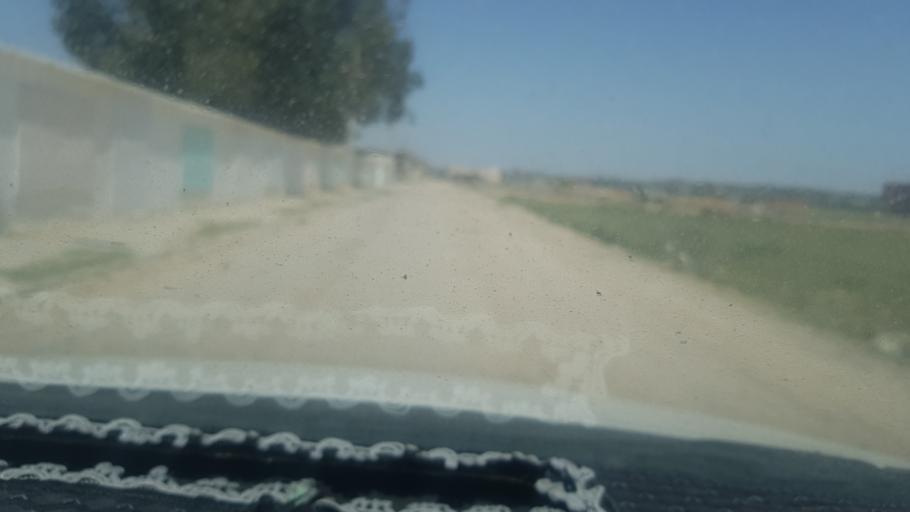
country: TN
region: Al Qayrawan
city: Kairouan
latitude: 35.6176
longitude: 9.9305
